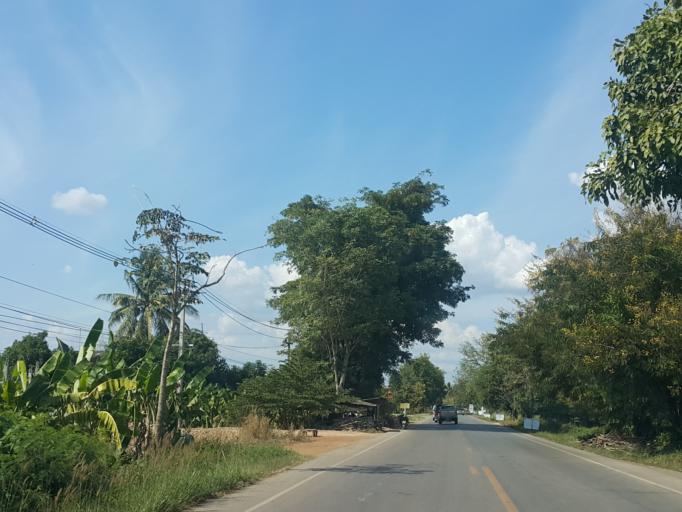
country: TH
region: Sukhothai
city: Sawankhalok
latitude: 17.2879
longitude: 99.8338
